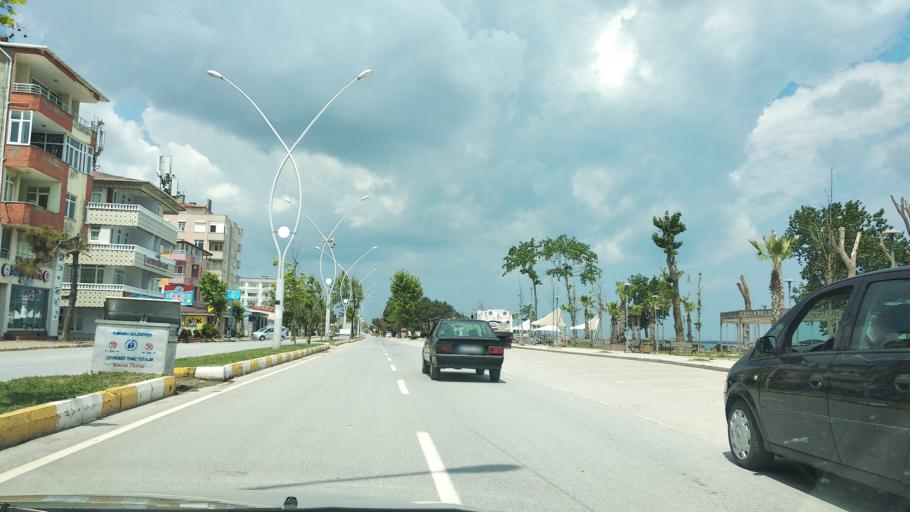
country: TR
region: Sakarya
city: Karasu
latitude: 41.1105
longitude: 30.6920
